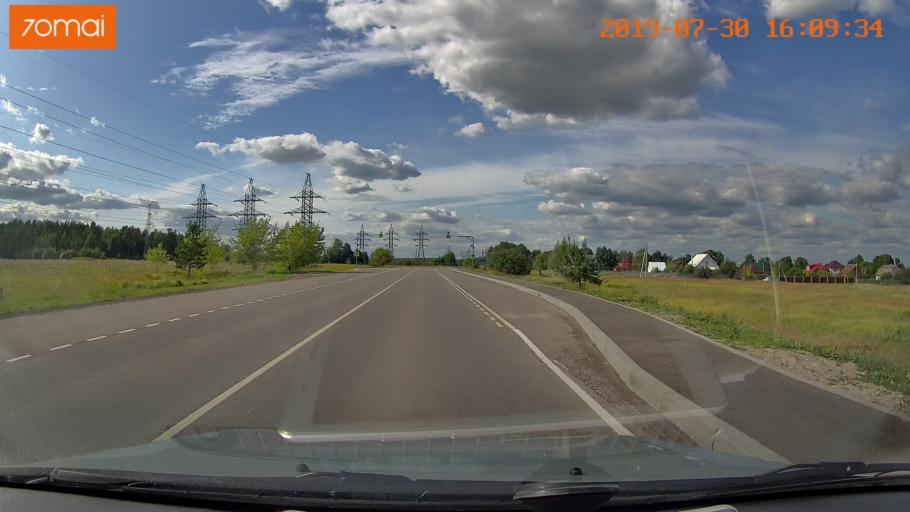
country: RU
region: Moskovskaya
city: Peski
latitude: 55.2543
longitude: 38.7179
